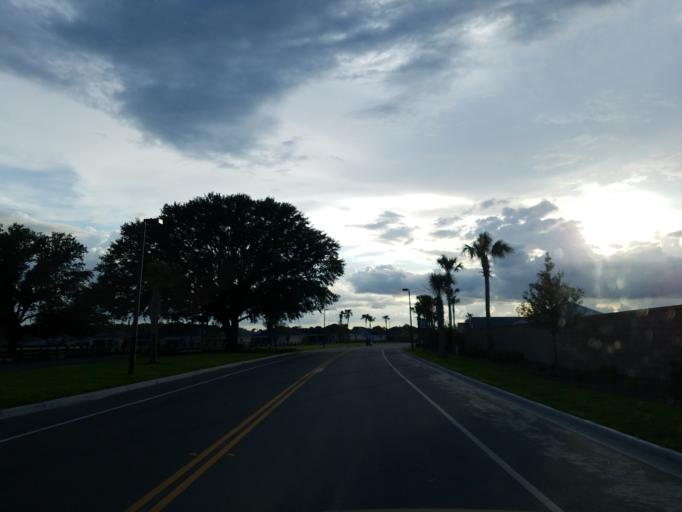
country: US
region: Florida
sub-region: Sumter County
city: Wildwood
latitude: 28.7898
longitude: -82.0122
